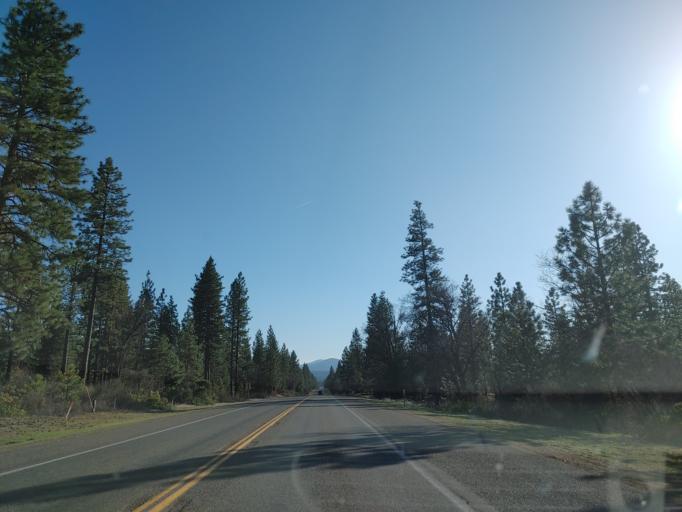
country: US
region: California
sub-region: Shasta County
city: Burney
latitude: 40.9104
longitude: -121.6340
